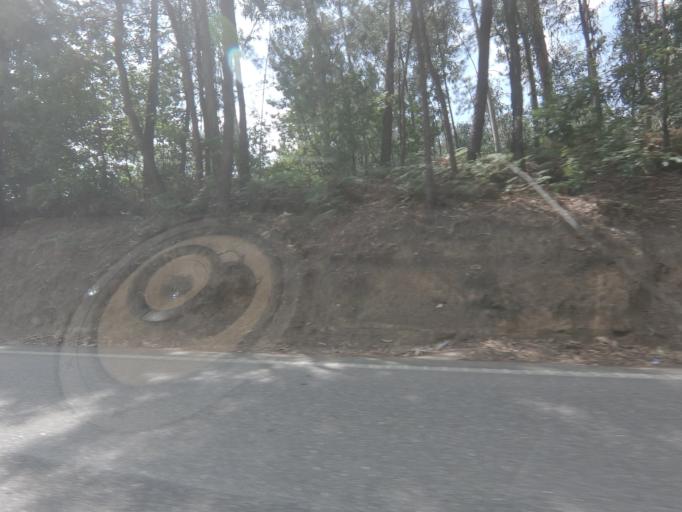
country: PT
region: Viana do Castelo
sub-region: Valenca
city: Valenca
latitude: 42.0316
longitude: -8.6710
